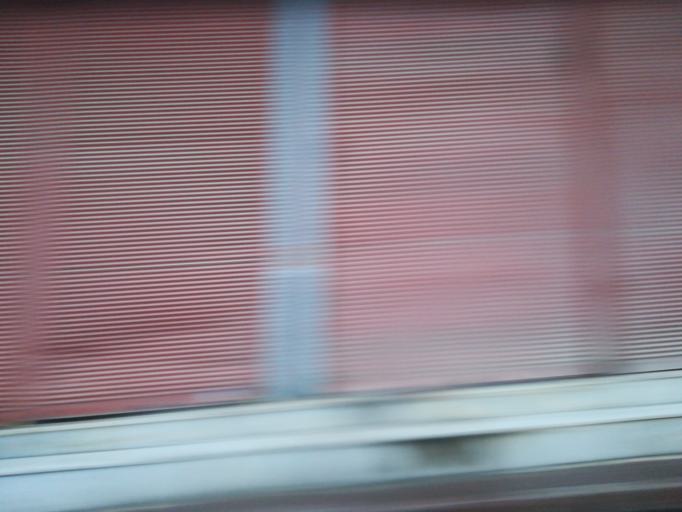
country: TR
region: Adana
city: Seyhan
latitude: 37.0035
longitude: 35.2799
